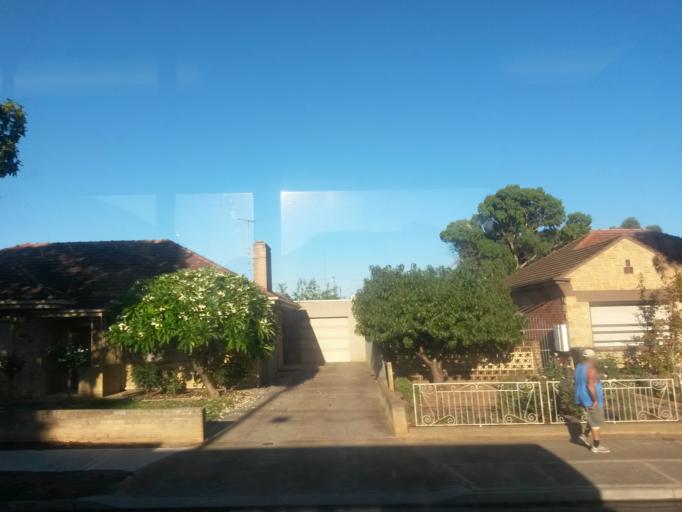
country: AU
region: South Australia
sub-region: Charles Sturt
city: Woodville
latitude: -34.8806
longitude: 138.5666
